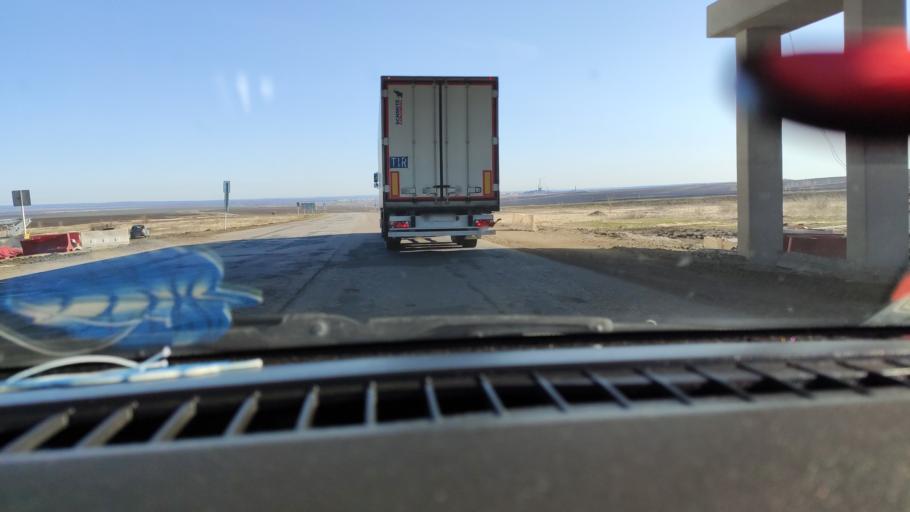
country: RU
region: Samara
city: Syzran'
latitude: 53.0009
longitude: 48.3296
